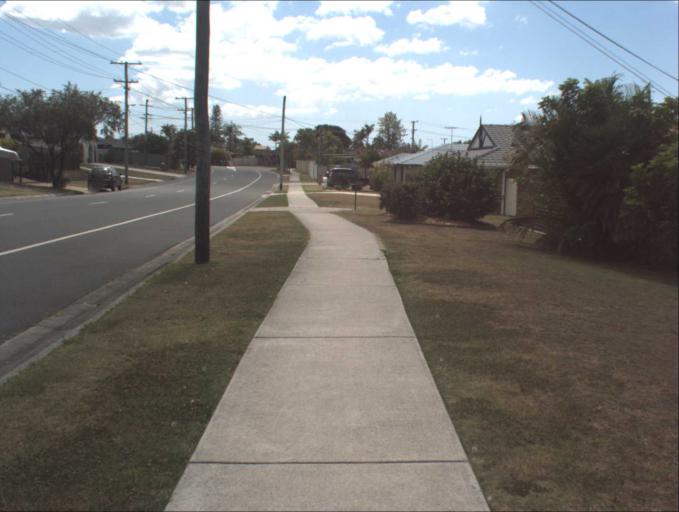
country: AU
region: Queensland
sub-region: Logan
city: Windaroo
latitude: -27.7335
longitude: 153.2116
